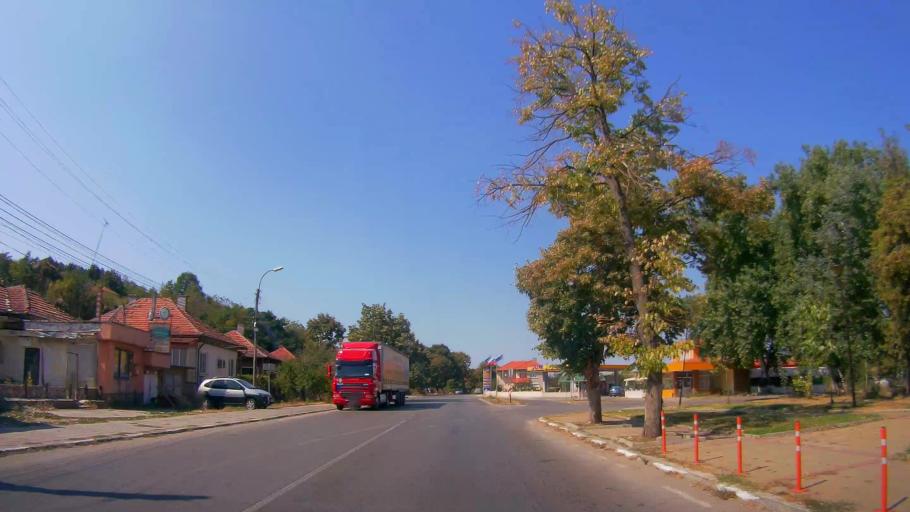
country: BG
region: Razgrad
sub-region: Obshtina Tsar Kaloyan
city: Tsar Kaloyan
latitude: 43.6089
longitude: 26.2367
